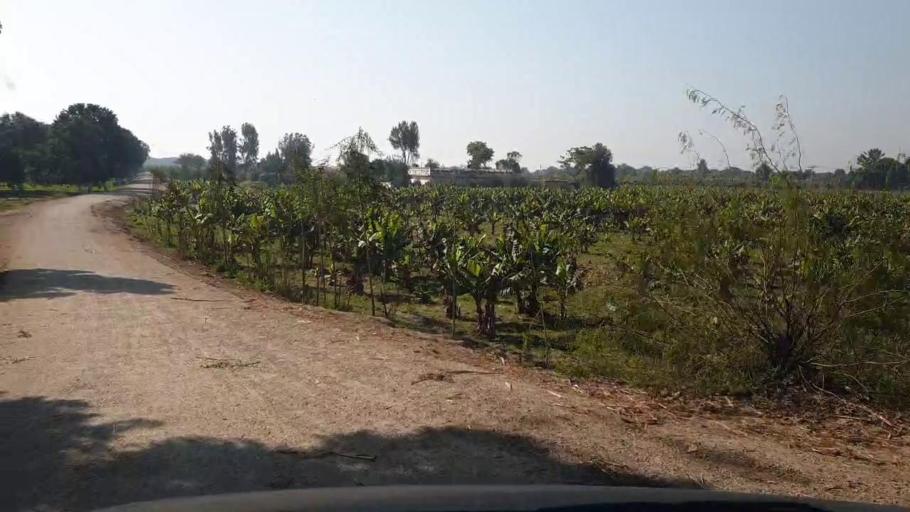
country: PK
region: Sindh
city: Tando Jam
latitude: 25.4444
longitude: 68.5977
